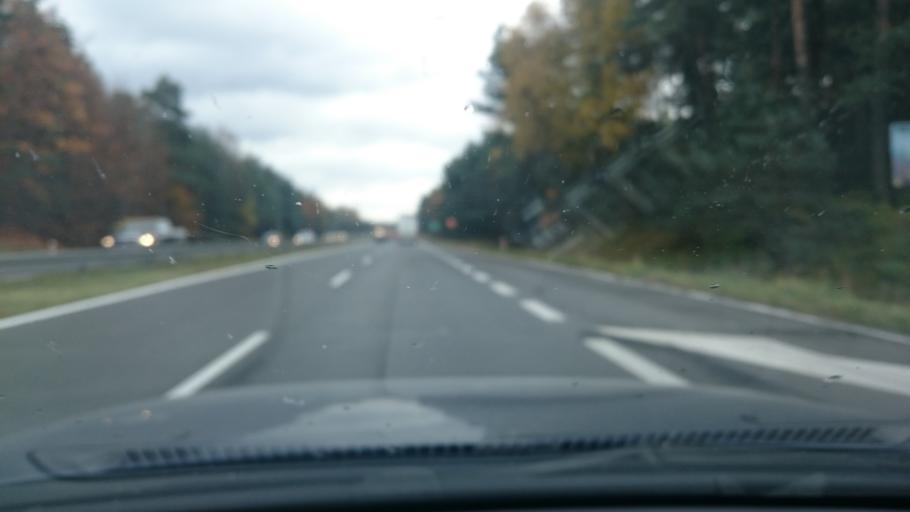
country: PL
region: Lesser Poland Voivodeship
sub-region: Powiat olkuski
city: Boleslaw
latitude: 50.2987
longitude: 19.4937
